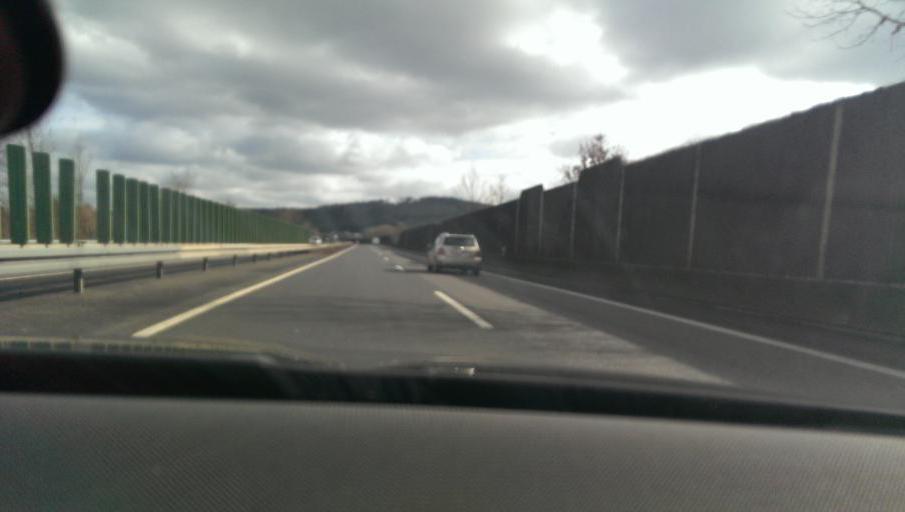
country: DE
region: Hesse
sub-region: Regierungsbezirk Darmstadt
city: Wachtersbach
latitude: 50.2245
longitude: 9.2624
